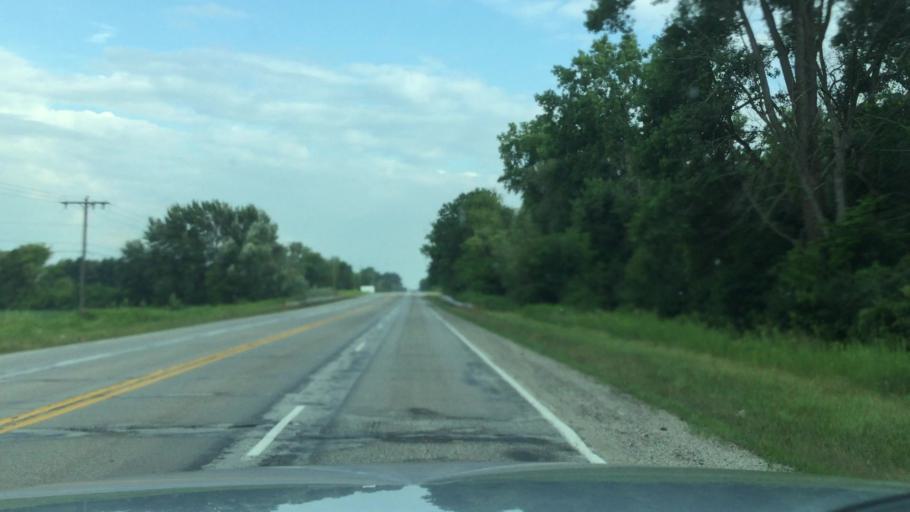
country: US
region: Michigan
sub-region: Saginaw County
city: Birch Run
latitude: 43.2711
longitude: -83.7852
